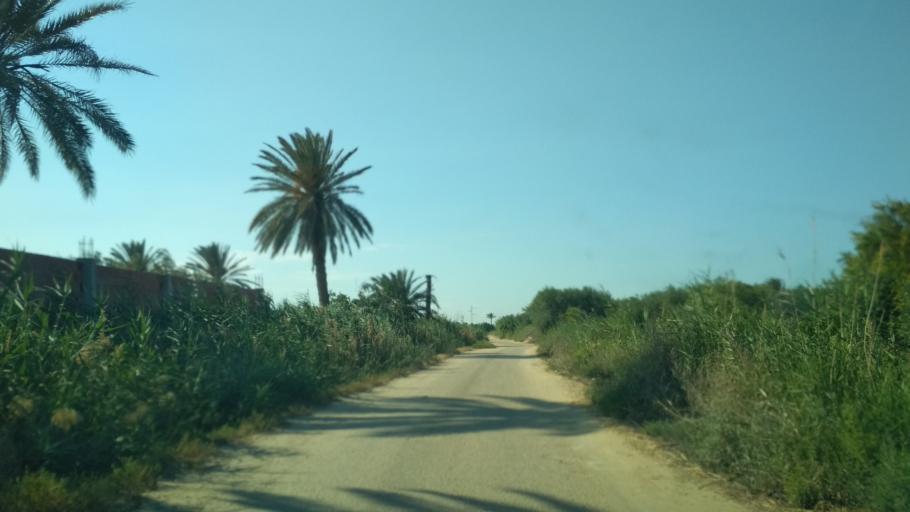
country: TN
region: Qabis
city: Gabes
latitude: 33.9573
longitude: 10.0587
